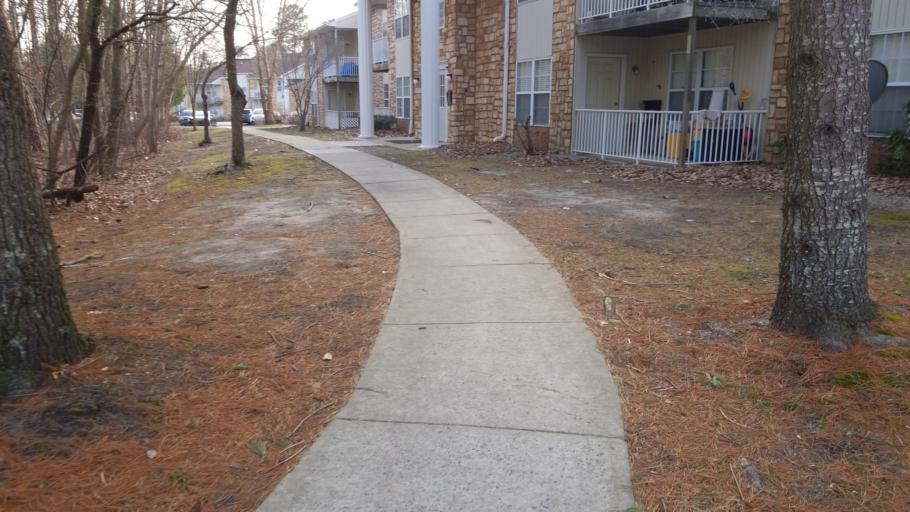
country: US
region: New Jersey
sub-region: Ocean County
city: Leisure Knoll
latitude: 39.9983
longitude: -74.2886
